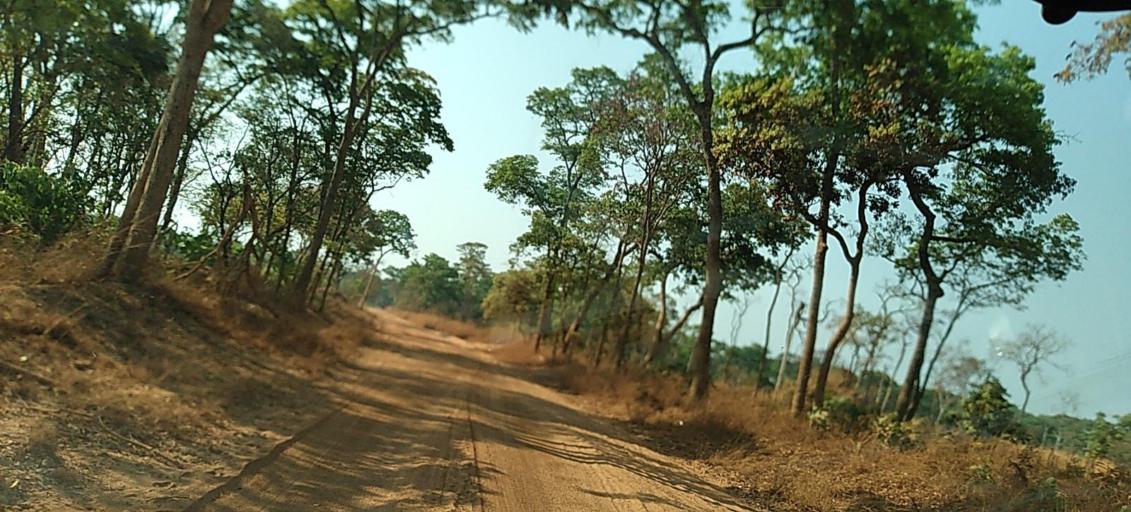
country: ZM
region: North-Western
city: Kasempa
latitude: -13.6482
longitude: 26.0023
